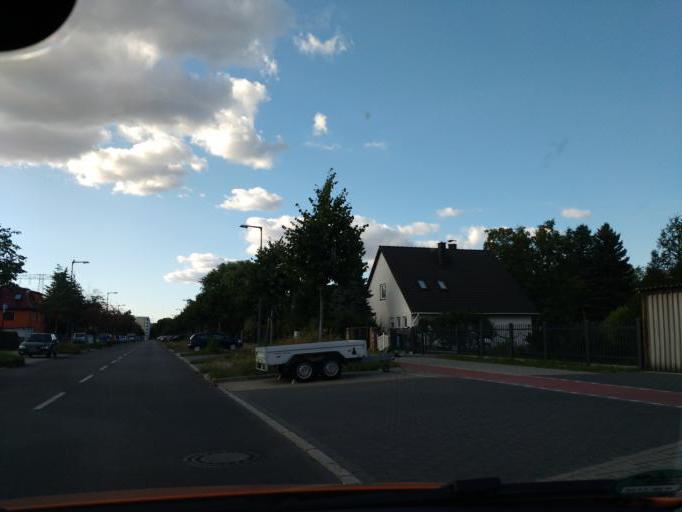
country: DE
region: Berlin
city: Johannisthal
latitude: 52.4322
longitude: 13.5059
